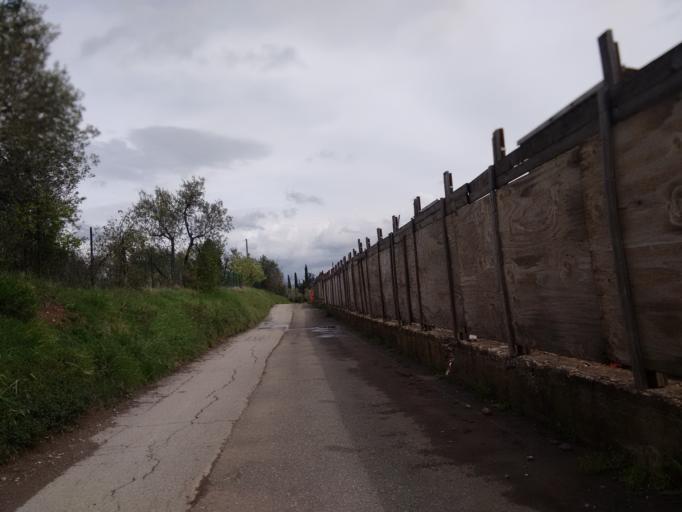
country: IT
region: Tuscany
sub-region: Province of Florence
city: Strada in Chianti
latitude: 43.6587
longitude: 11.3071
